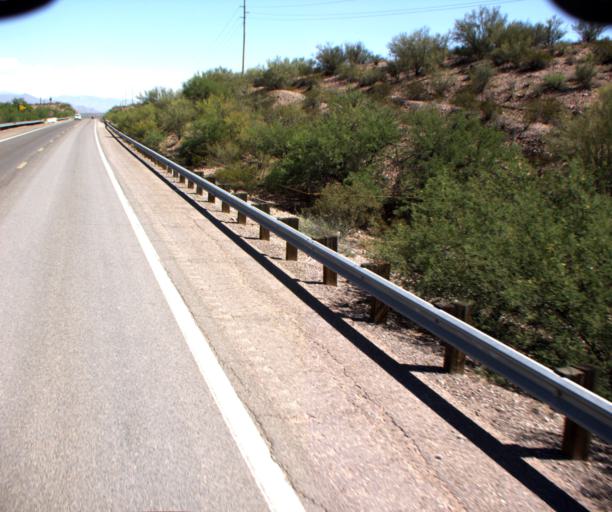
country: US
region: Arizona
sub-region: Pinal County
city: Mammoth
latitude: 32.8894
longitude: -110.7160
